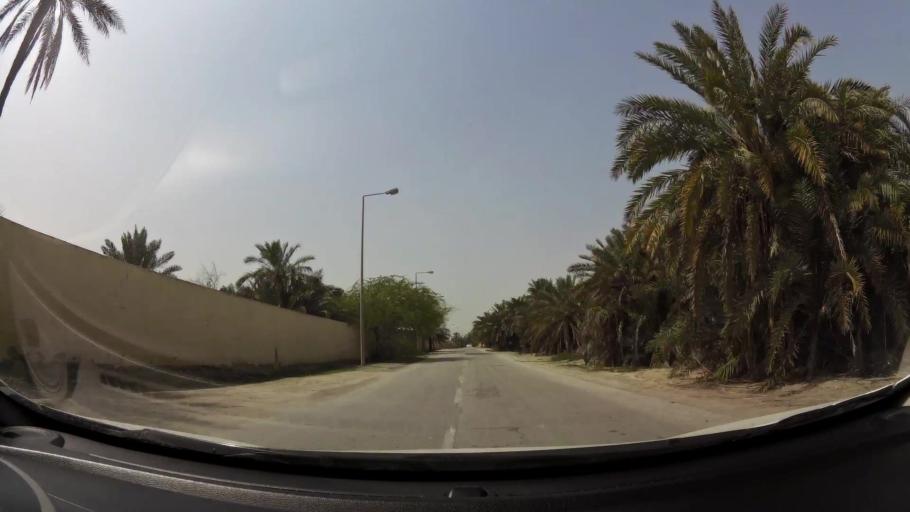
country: BH
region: Manama
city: Jidd Hafs
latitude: 26.2299
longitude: 50.4706
